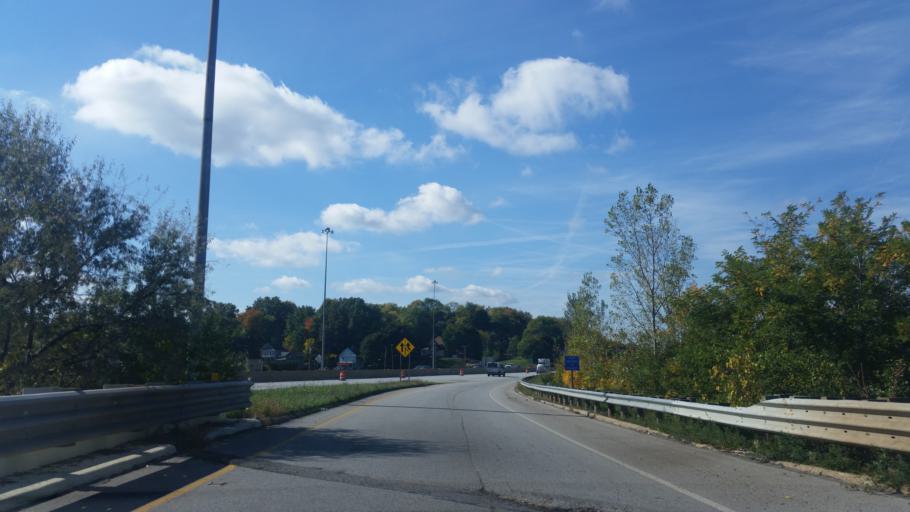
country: US
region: Ohio
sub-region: Summit County
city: Akron
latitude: 41.0627
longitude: -81.5272
